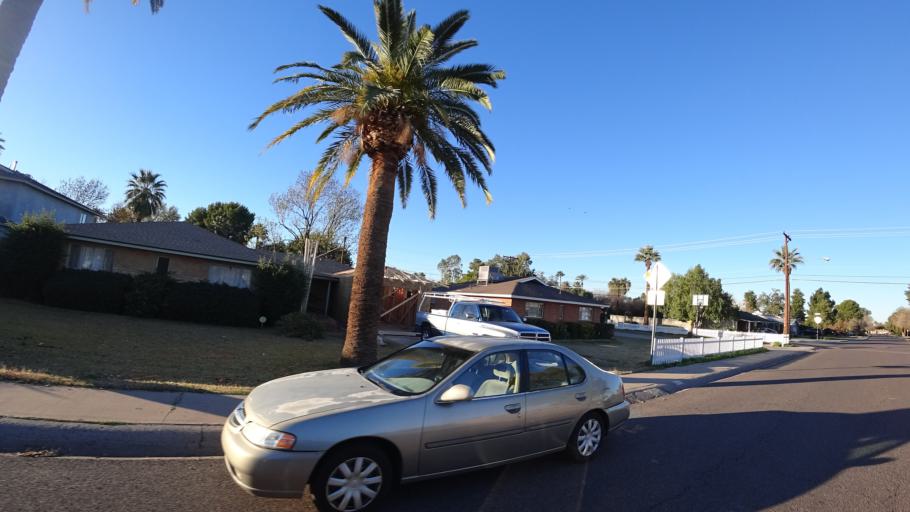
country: US
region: Arizona
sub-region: Maricopa County
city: Paradise Valley
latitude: 33.4918
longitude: -111.9993
